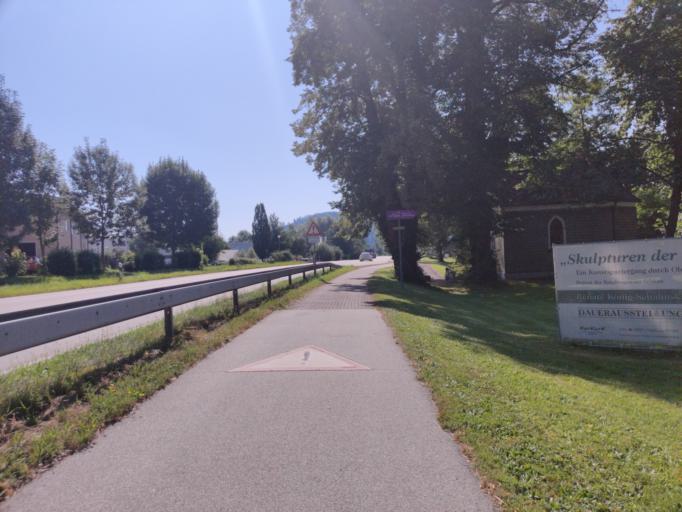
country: DE
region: Bavaria
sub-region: Lower Bavaria
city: Obernzell
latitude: 48.5596
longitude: 13.6220
